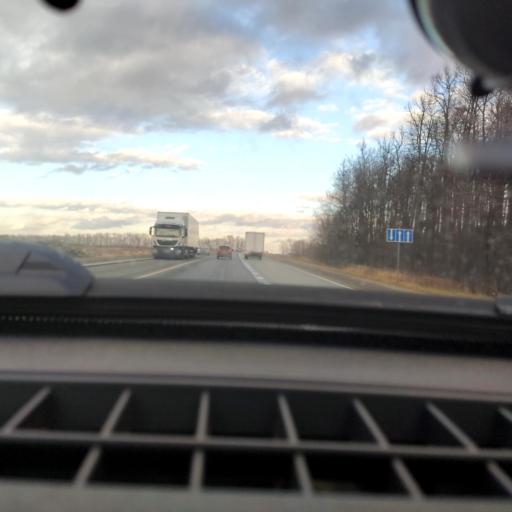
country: RU
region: Bashkortostan
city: Iglino
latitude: 54.7254
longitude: 56.2468
